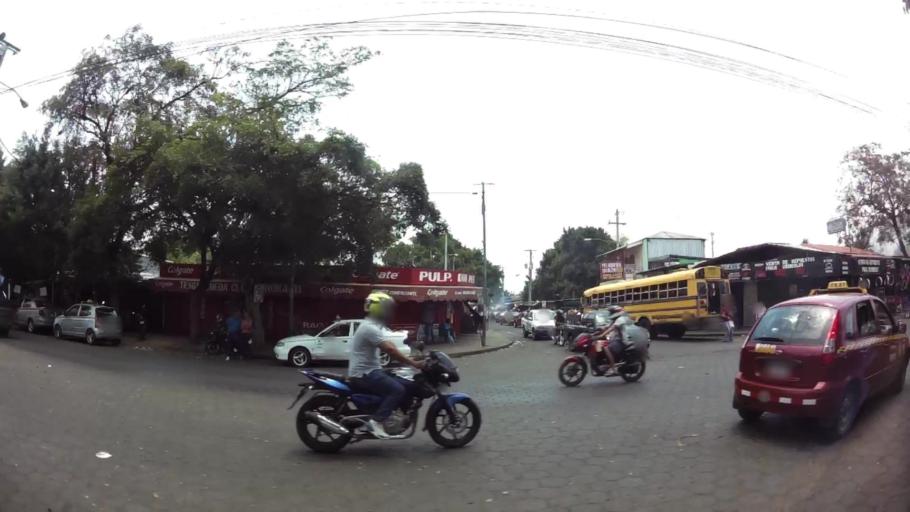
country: NI
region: Managua
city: Managua
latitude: 12.1275
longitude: -86.3014
